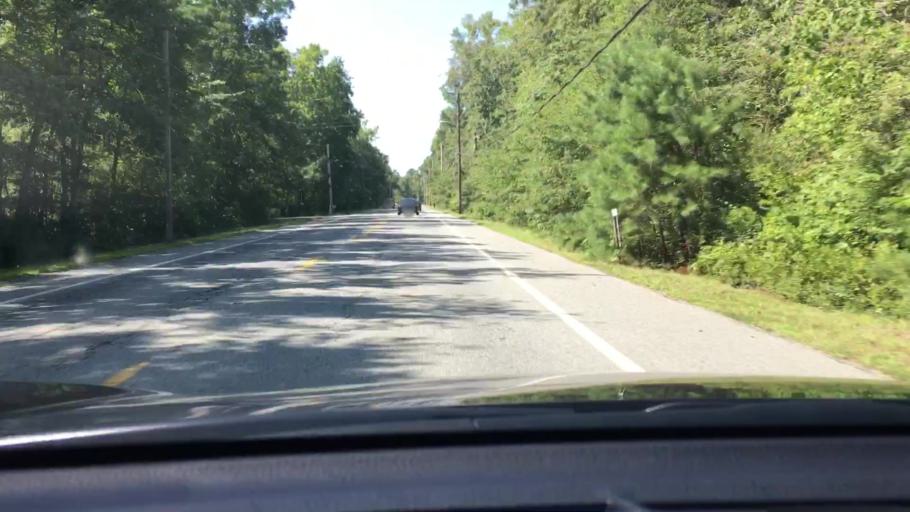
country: US
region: New Jersey
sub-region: Cape May County
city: Woodbine
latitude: 39.2891
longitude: -74.7878
